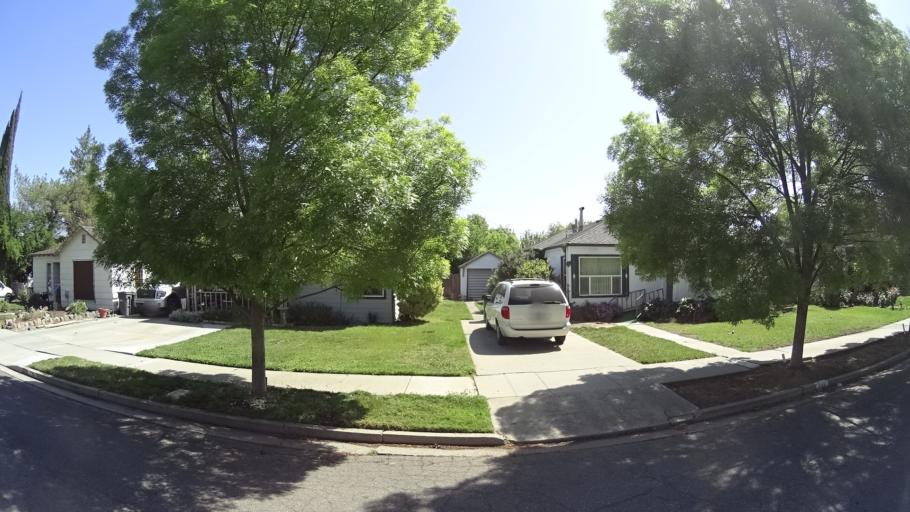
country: US
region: California
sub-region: Glenn County
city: Willows
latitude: 39.5182
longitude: -122.2009
